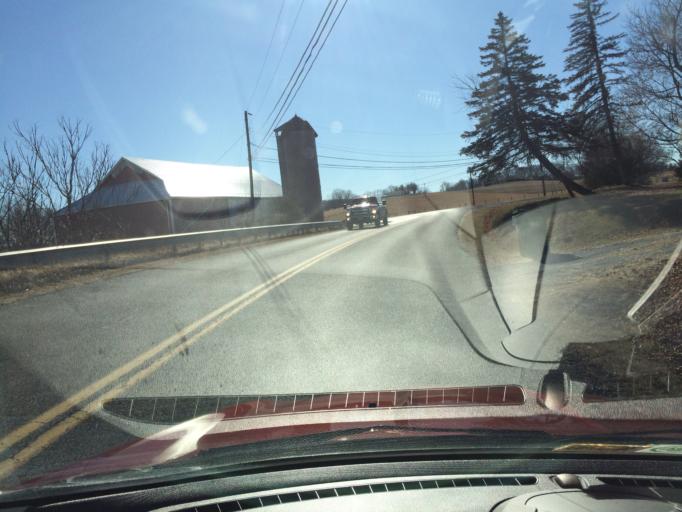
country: US
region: Virginia
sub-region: Rockingham County
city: Bridgewater
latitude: 38.3714
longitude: -78.9787
